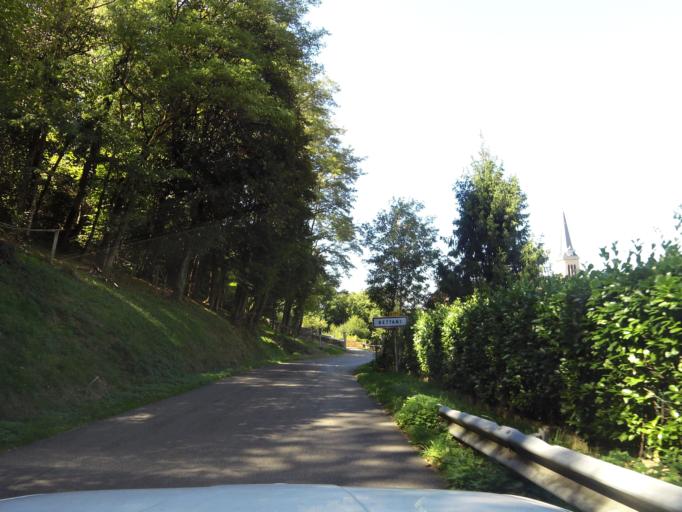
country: FR
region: Rhone-Alpes
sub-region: Departement de l'Ain
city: Vaux-en-Bugey
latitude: 45.9419
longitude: 5.3644
